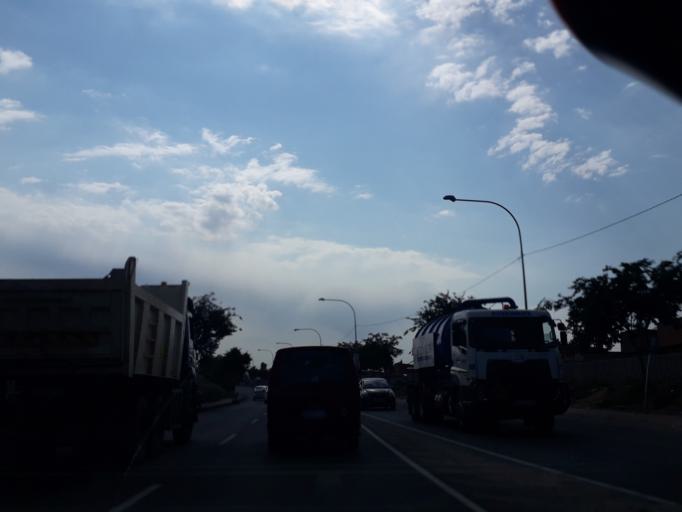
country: ZA
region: Gauteng
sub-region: City of Johannesburg Metropolitan Municipality
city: Modderfontein
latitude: -26.1062
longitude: 28.1182
